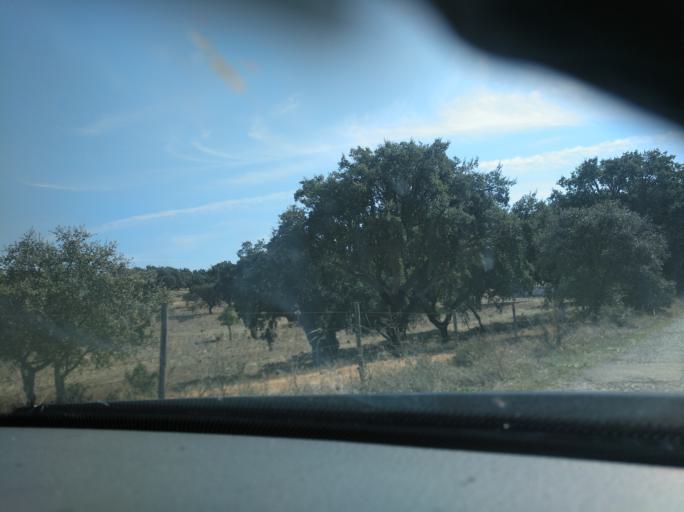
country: PT
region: Evora
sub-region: Arraiolos
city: Arraiolos
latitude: 38.7071
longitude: -8.0993
